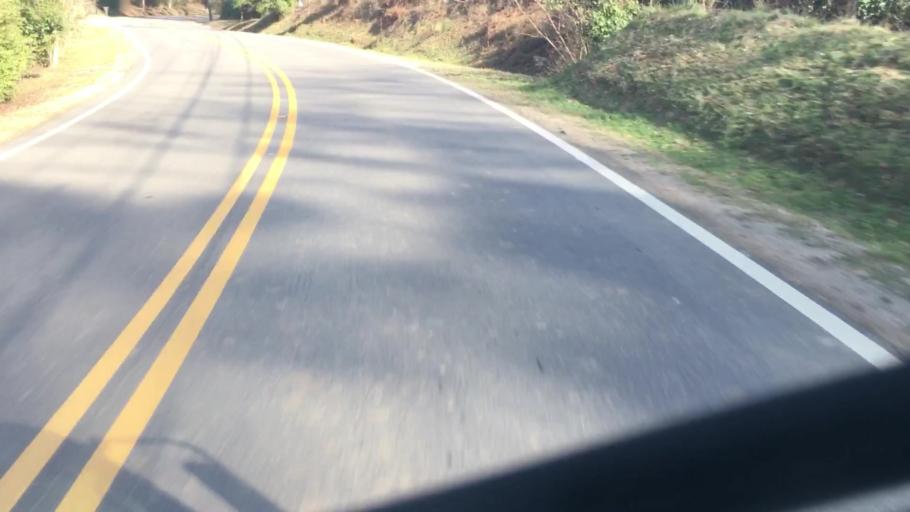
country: US
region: Alabama
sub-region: Jefferson County
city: Cahaba Heights
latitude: 33.4512
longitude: -86.7137
